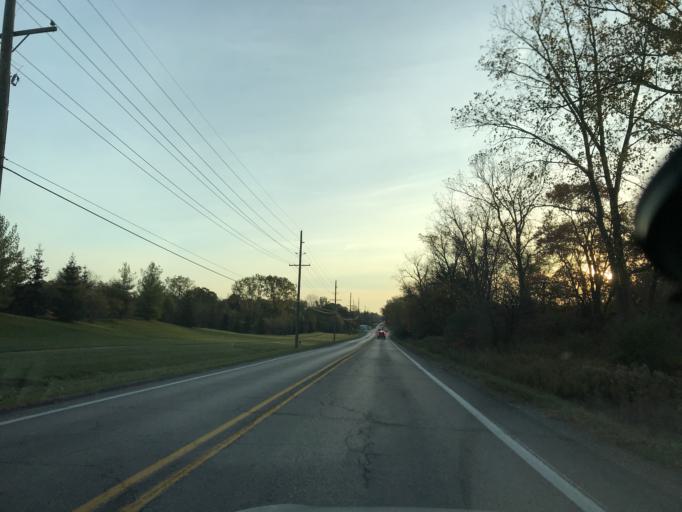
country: US
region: Michigan
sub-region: Oakland County
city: Wixom
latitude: 42.4645
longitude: -83.5386
